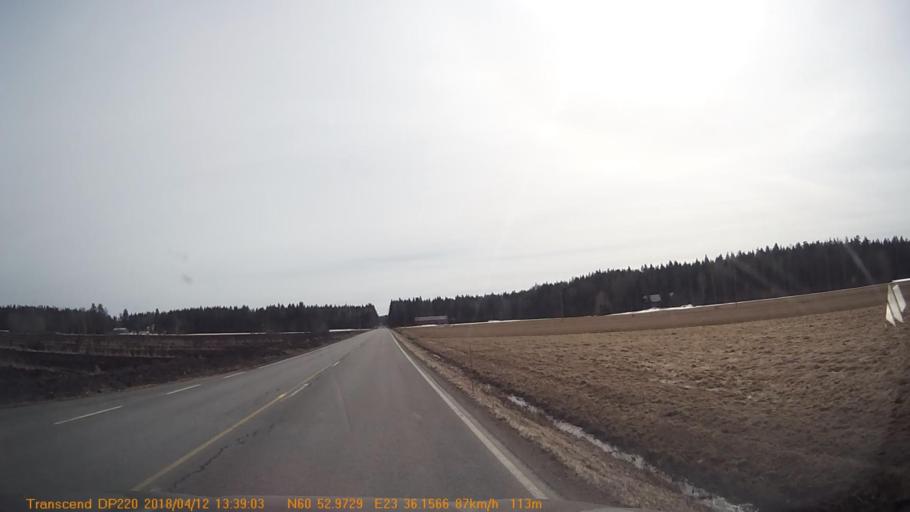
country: FI
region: Haeme
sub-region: Forssa
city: Forssa
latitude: 60.8826
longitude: 23.6027
